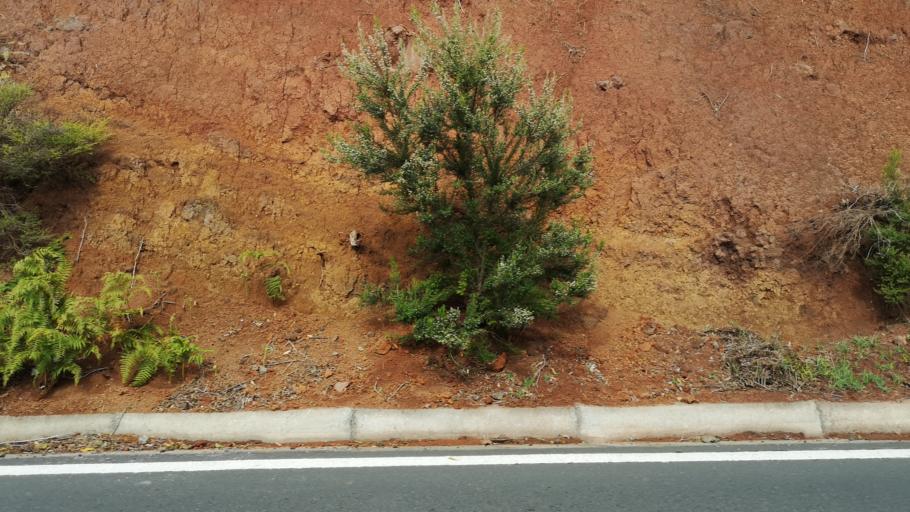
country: ES
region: Canary Islands
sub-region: Provincia de Santa Cruz de Tenerife
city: Alajero
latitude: 28.1112
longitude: -17.2410
